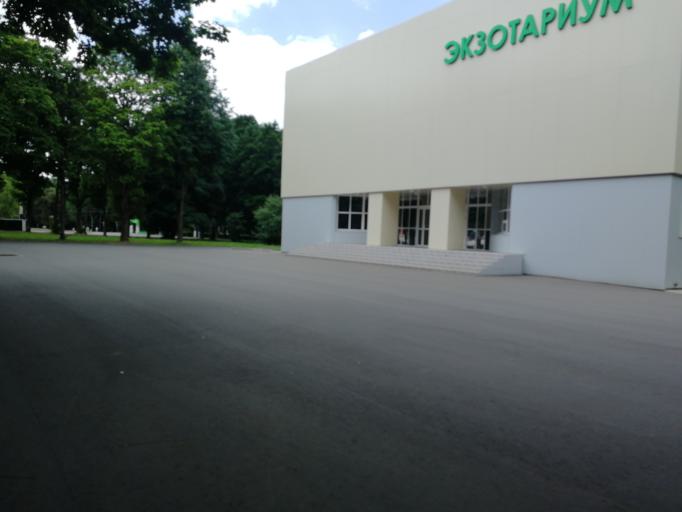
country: RU
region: Tula
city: Tula
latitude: 54.1810
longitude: 37.5896
